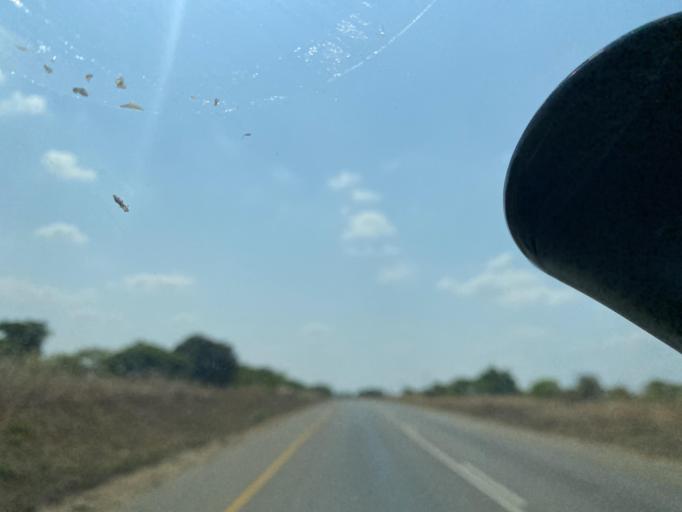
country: ZM
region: Lusaka
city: Chongwe
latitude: -15.5372
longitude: 28.6524
